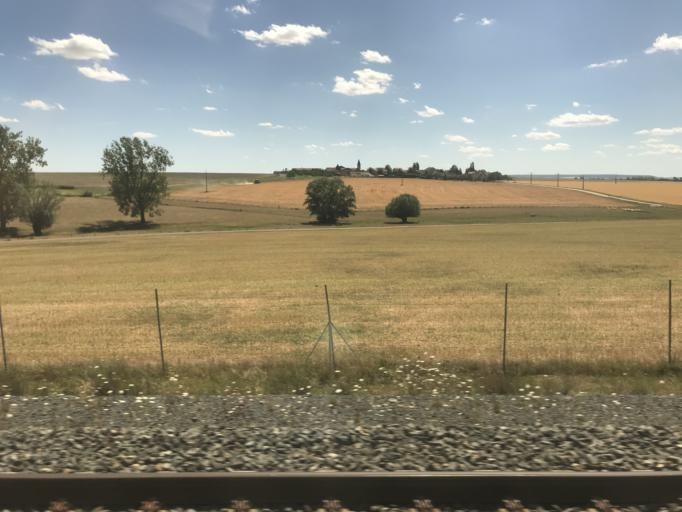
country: FR
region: Lorraine
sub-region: Departement de la Moselle
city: Verny
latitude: 48.9584
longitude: 6.2328
